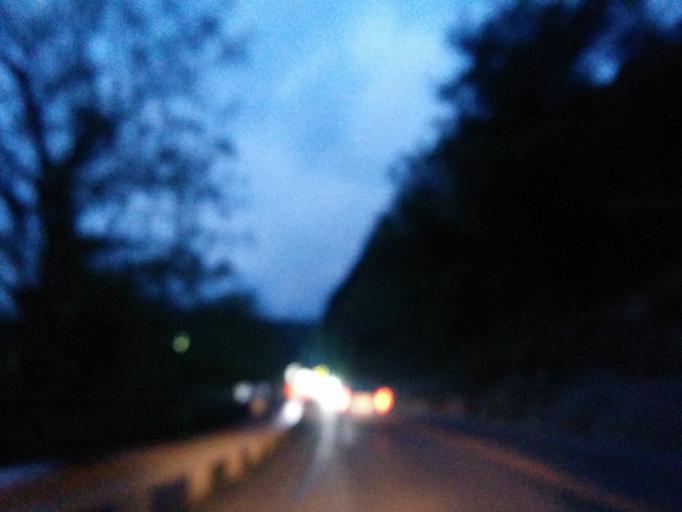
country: JP
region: Gifu
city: Mino
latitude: 35.5689
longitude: 136.9240
